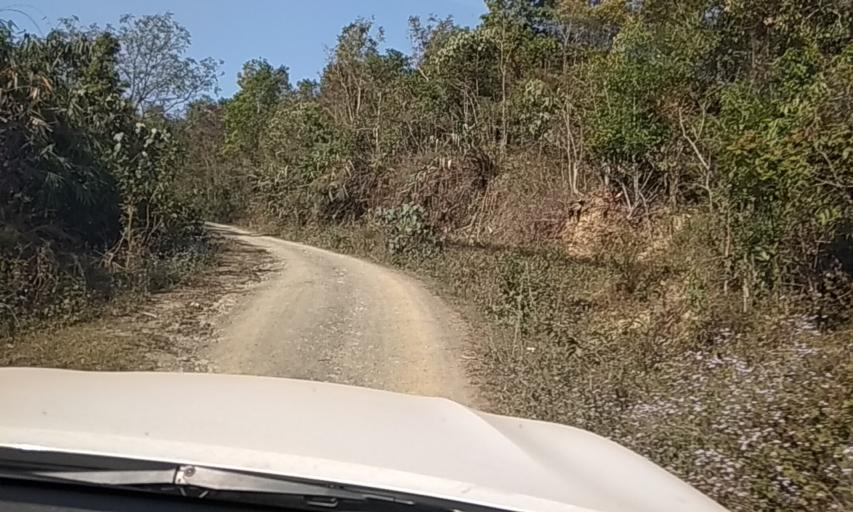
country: LA
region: Phongsali
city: Phongsali
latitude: 21.6944
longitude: 102.0870
